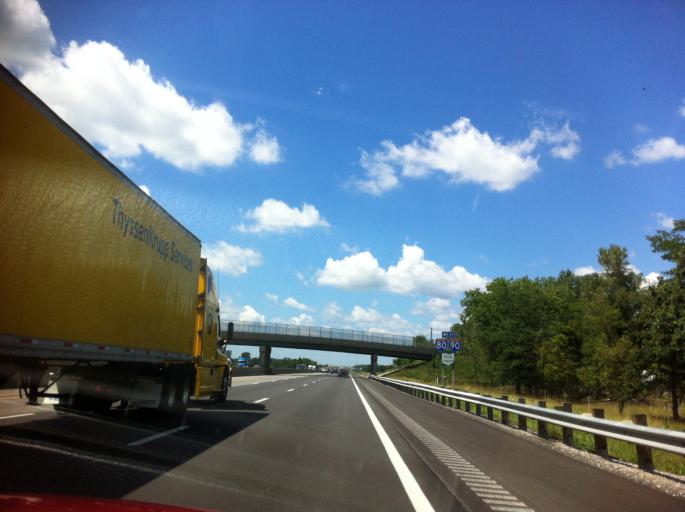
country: US
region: Ohio
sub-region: Ottawa County
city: Genoa
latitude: 41.4939
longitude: -83.3763
